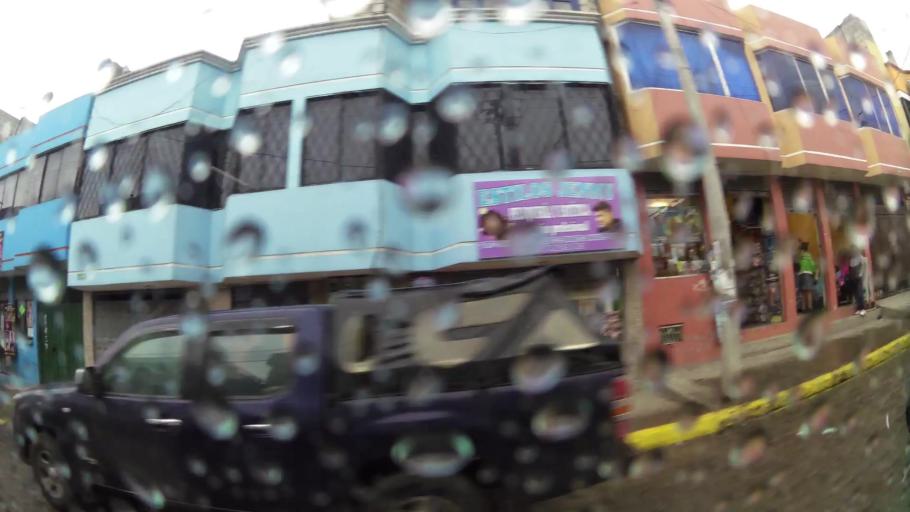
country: EC
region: Pichincha
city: Quito
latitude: -0.3181
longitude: -78.5553
